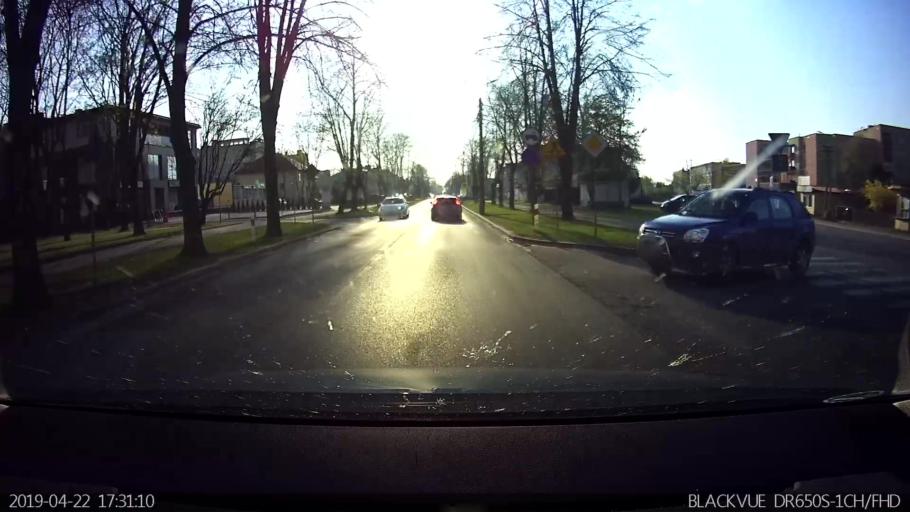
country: PL
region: Masovian Voivodeship
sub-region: Powiat sokolowski
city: Sokolow Podlaski
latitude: 52.4071
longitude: 22.2409
